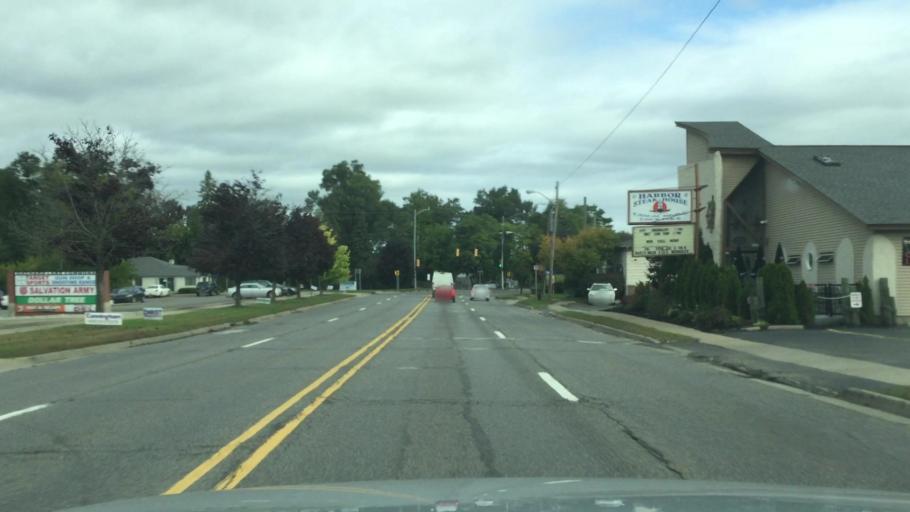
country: US
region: Michigan
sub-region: Oakland County
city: Keego Harbor
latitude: 42.6027
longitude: -83.3487
